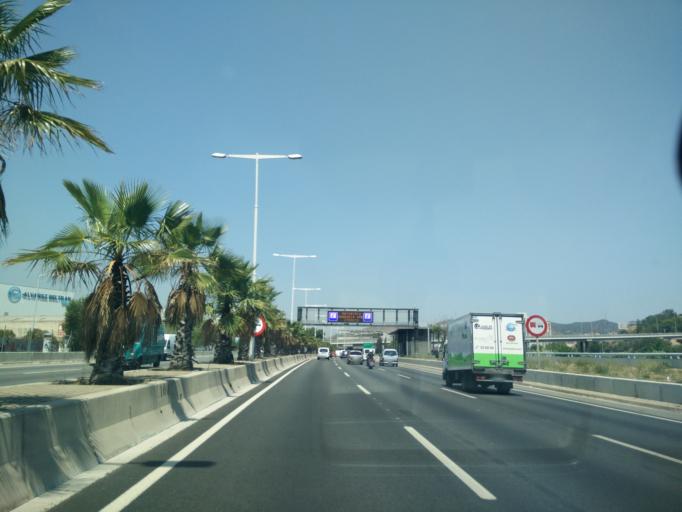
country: ES
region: Catalonia
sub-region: Provincia de Barcelona
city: Sant Adria de Besos
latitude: 41.4332
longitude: 2.2106
